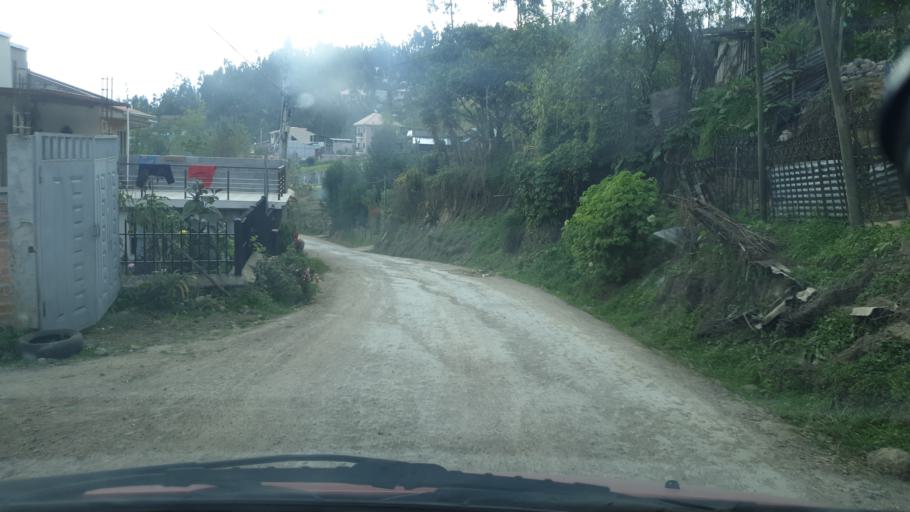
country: EC
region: Azuay
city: Cuenca
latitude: -2.9195
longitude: -78.9758
